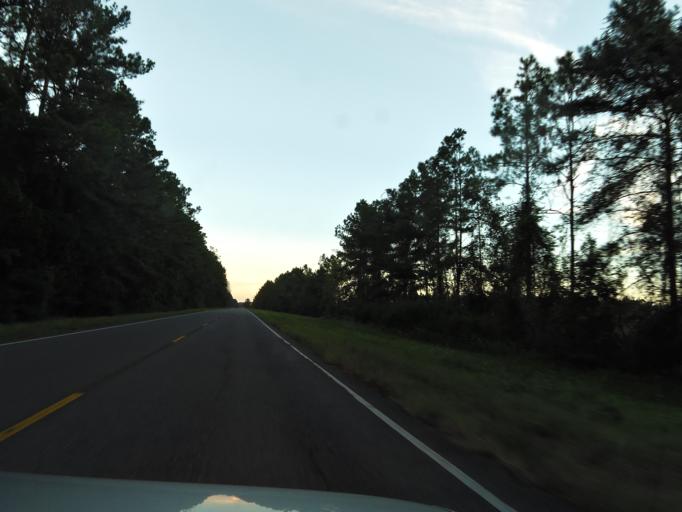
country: US
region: Georgia
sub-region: Camden County
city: Kingsland
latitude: 30.7604
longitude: -81.6873
